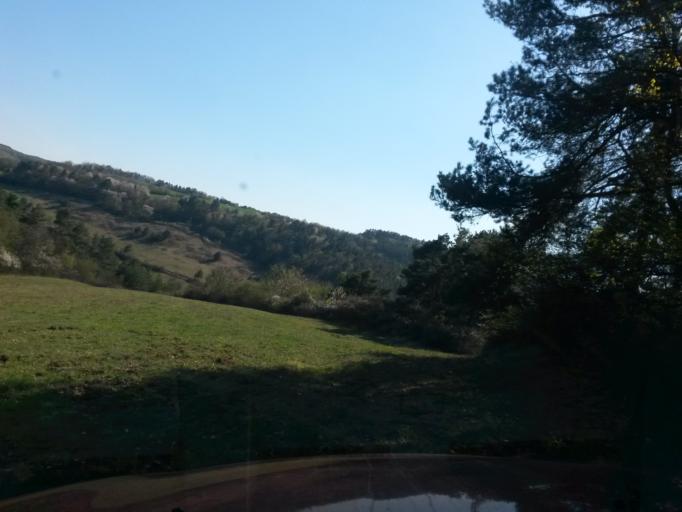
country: SK
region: Presovsky
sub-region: Okres Presov
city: Presov
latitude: 48.9631
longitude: 21.1105
